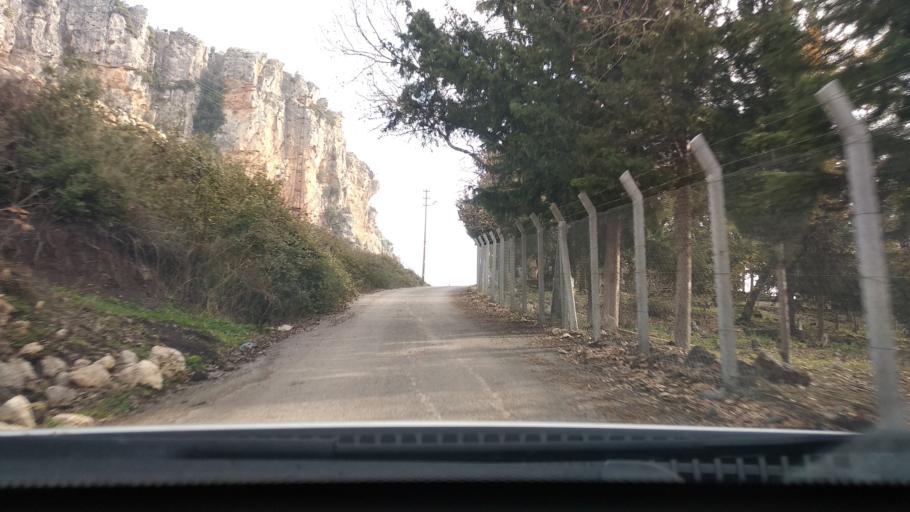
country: TR
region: Mersin
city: Kuzucubelen
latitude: 36.8759
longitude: 34.4722
